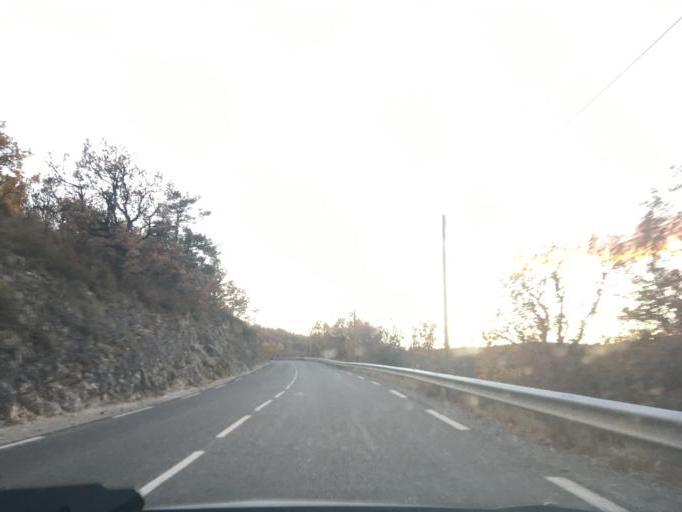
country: FR
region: Provence-Alpes-Cote d'Azur
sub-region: Departement du Var
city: Montferrat
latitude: 43.6741
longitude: 6.4967
